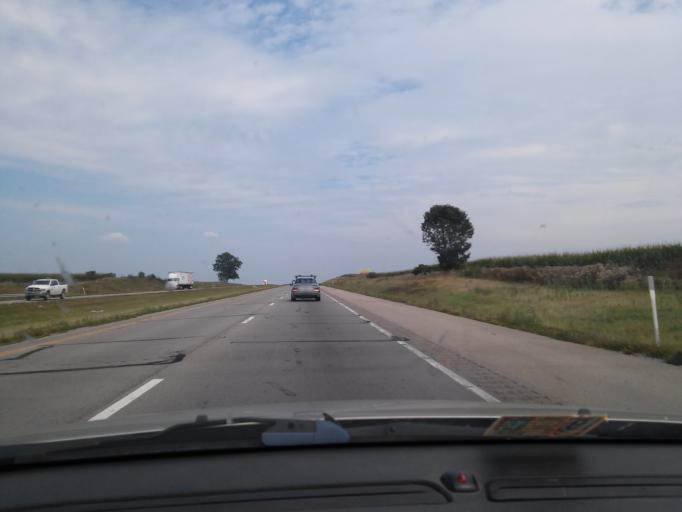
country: US
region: Indiana
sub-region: Wayne County
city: Cambridge City
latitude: 39.8532
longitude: -85.1945
